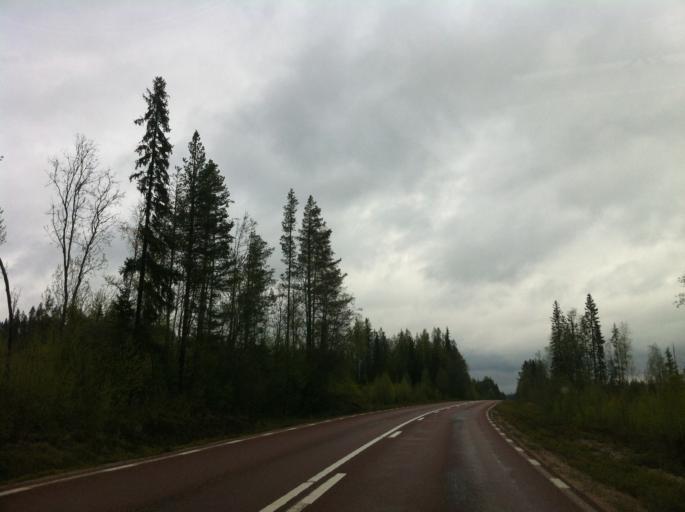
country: SE
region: Jaemtland
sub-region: Harjedalens Kommun
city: Sveg
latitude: 61.8742
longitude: 14.6293
